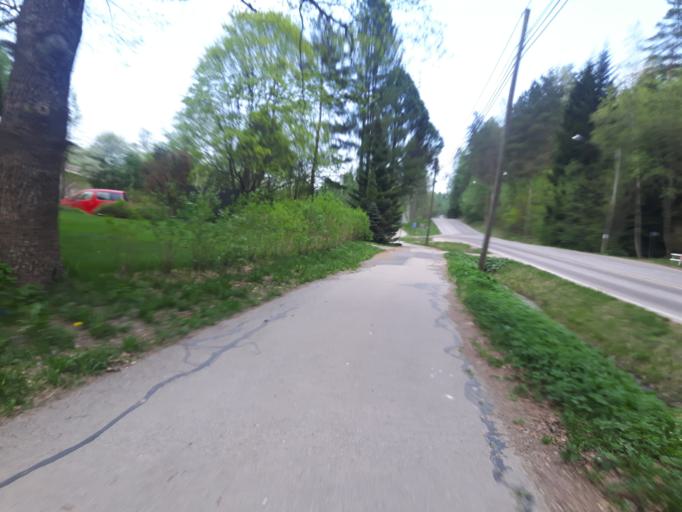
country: FI
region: Uusimaa
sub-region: Porvoo
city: Porvoo
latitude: 60.4015
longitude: 25.7228
